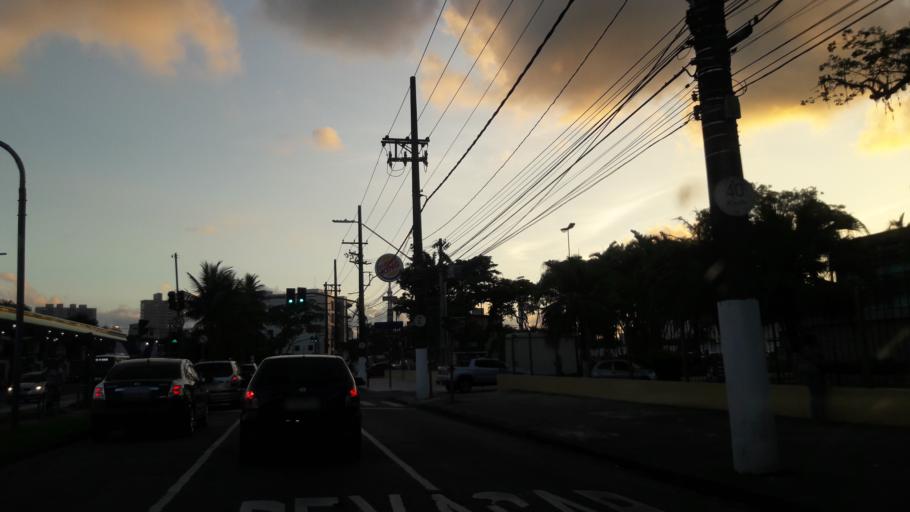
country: BR
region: Sao Paulo
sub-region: Santos
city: Santos
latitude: -23.9453
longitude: -46.3354
